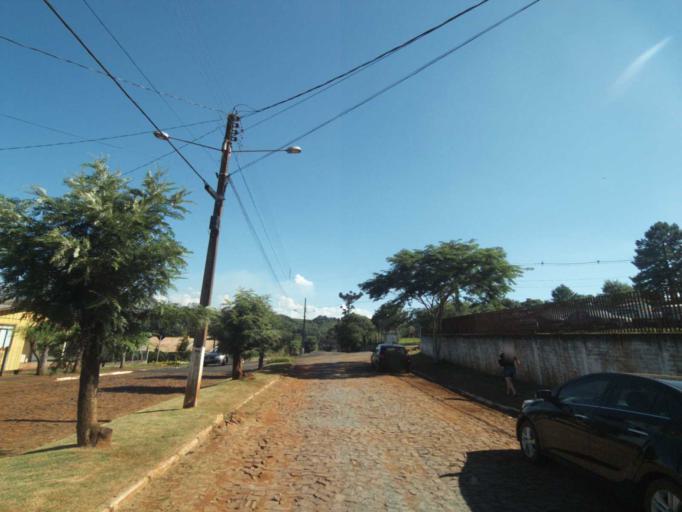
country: BR
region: Parana
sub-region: Laranjeiras Do Sul
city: Laranjeiras do Sul
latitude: -25.3835
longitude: -52.2033
